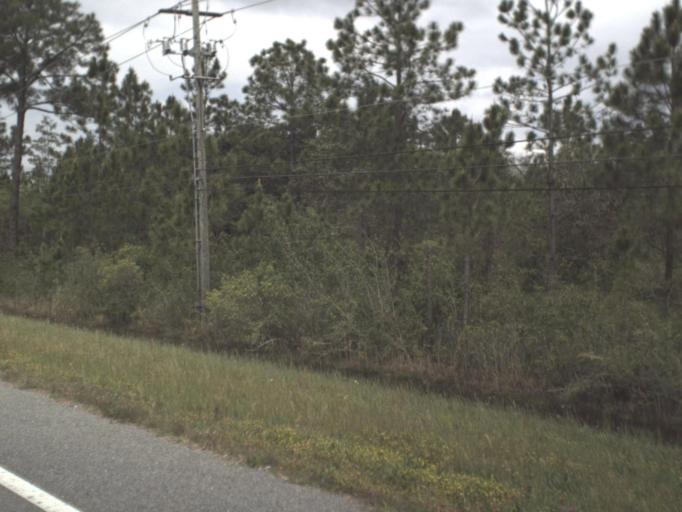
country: US
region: Florida
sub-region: Escambia County
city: Myrtle Grove
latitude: 30.4028
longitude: -87.3230
